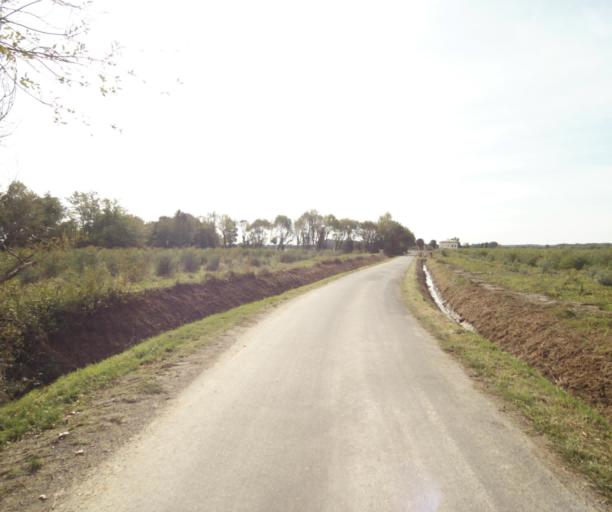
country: FR
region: Midi-Pyrenees
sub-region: Departement du Tarn-et-Garonne
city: Labastide-Saint-Pierre
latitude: 43.8978
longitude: 1.3592
